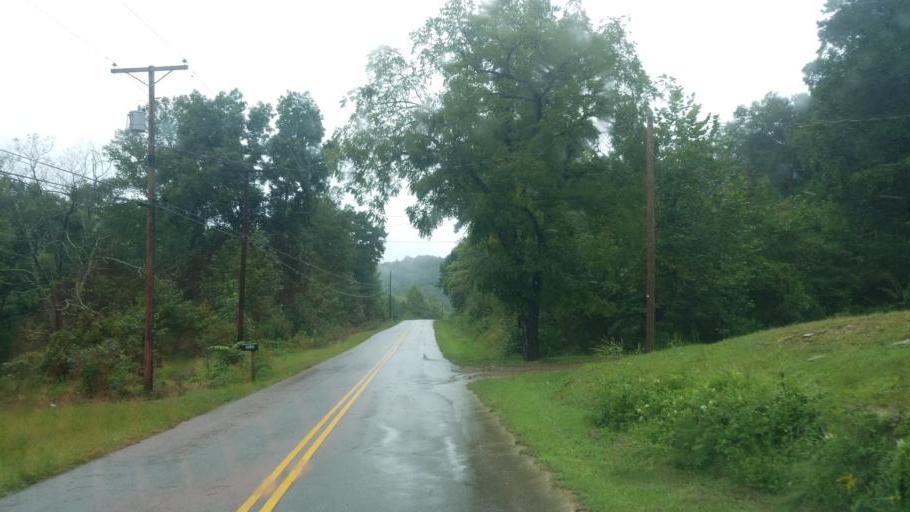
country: US
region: Ohio
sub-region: Scioto County
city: West Portsmouth
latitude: 38.7474
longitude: -83.0911
